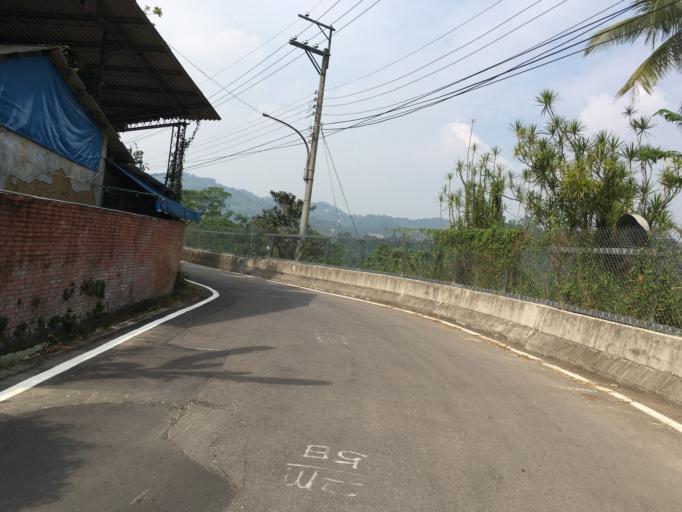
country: TW
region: Taiwan
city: Fengyuan
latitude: 24.1866
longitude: 120.7513
